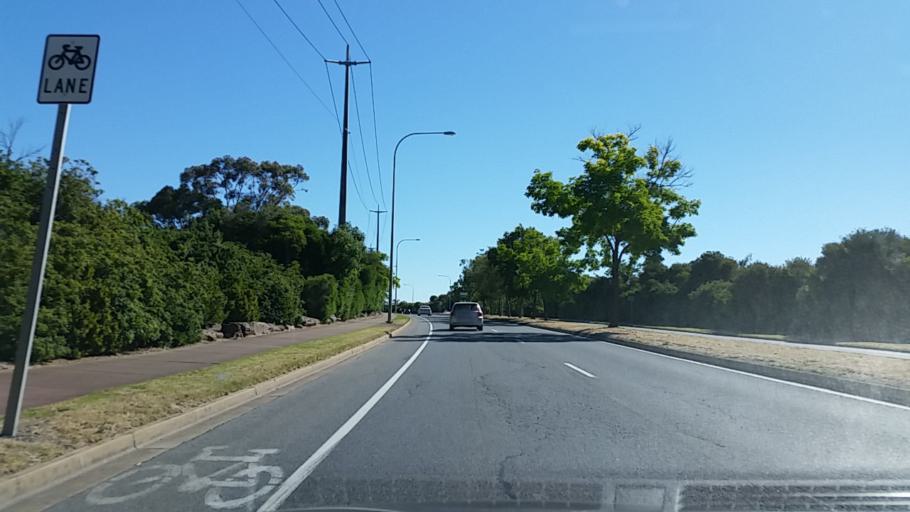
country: AU
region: South Australia
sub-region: Tea Tree Gully
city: Modbury
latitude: -34.7956
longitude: 138.6885
